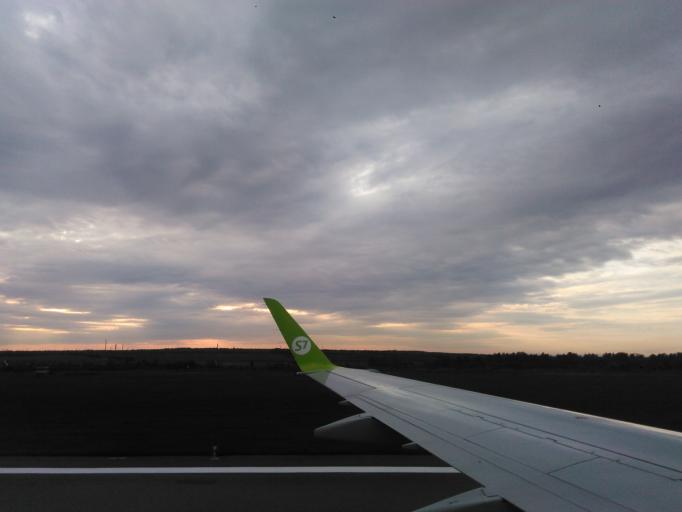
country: RU
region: Tatarstan
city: Yelabuga
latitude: 55.5661
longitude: 52.0972
